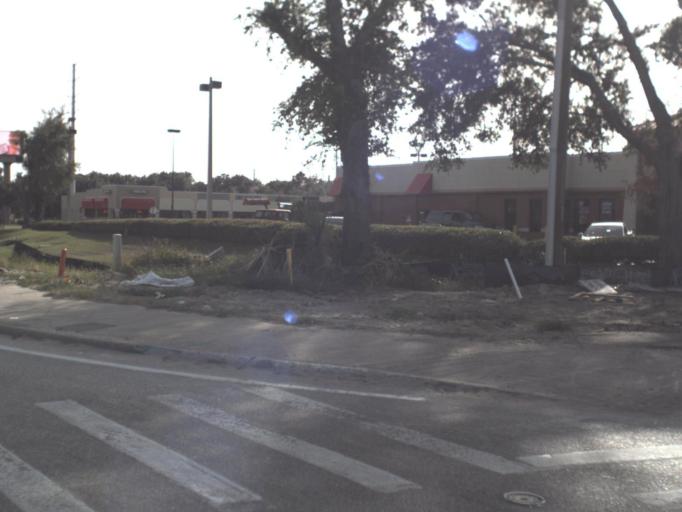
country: US
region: Florida
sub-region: Orange County
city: Alafaya
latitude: 28.5668
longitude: -81.2078
